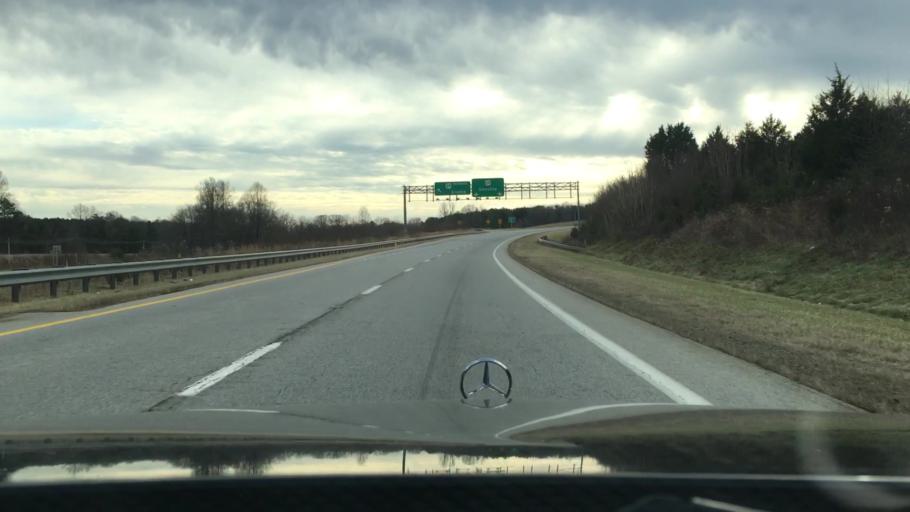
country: US
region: Virginia
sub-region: Pittsylvania County
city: Gretna
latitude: 36.9803
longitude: -79.3546
